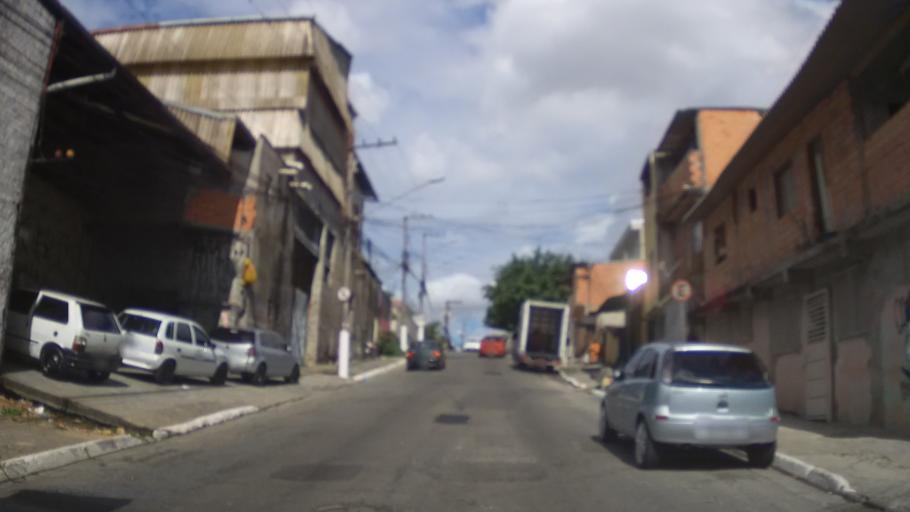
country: BR
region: Sao Paulo
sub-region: Guarulhos
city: Guarulhos
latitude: -23.4856
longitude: -46.5563
